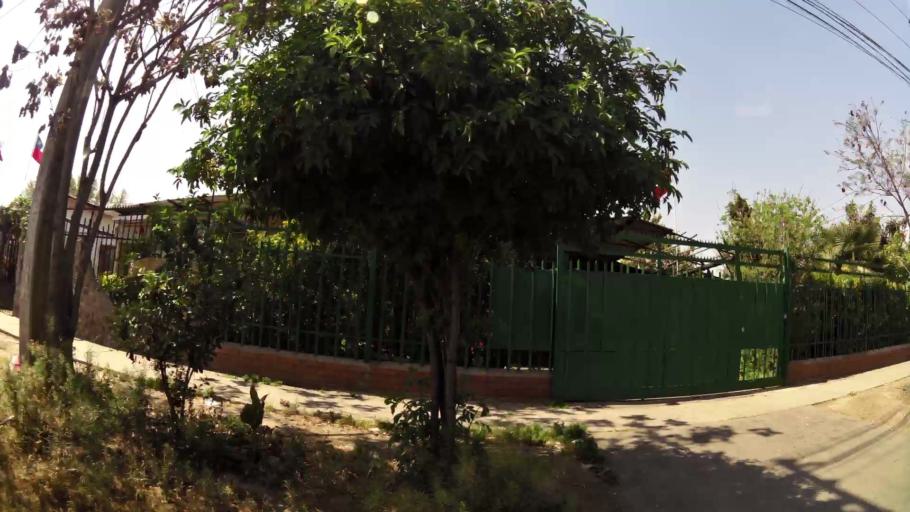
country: CL
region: Santiago Metropolitan
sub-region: Provincia de Santiago
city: La Pintana
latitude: -33.5475
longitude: -70.6145
